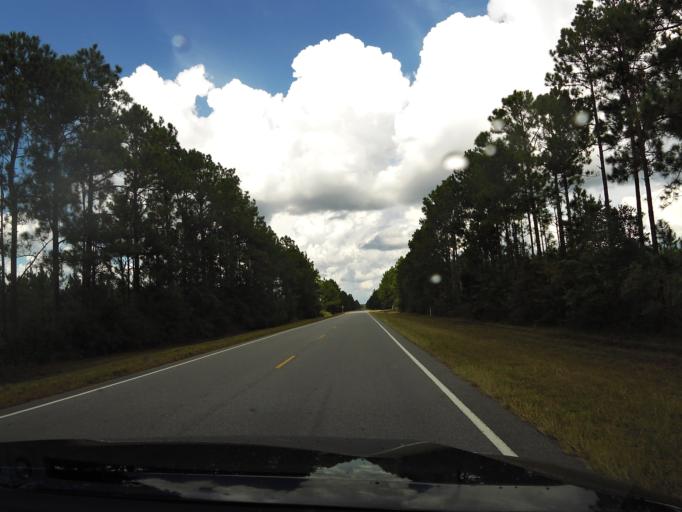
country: US
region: Georgia
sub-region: Charlton County
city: Folkston
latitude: 30.9085
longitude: -82.0184
